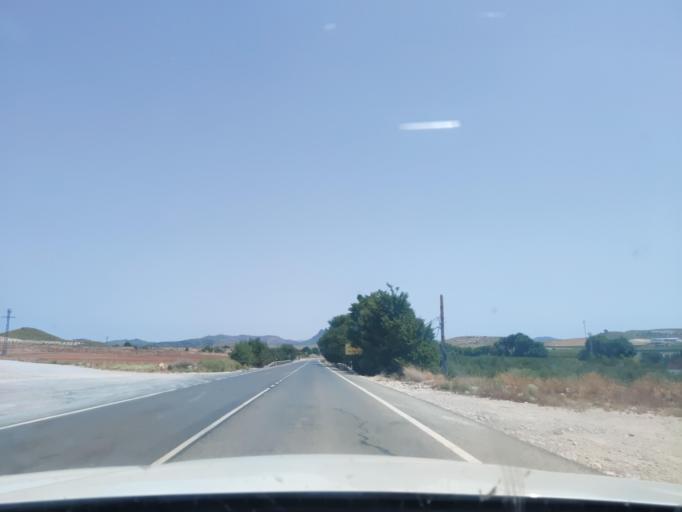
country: ES
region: Castille-La Mancha
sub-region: Provincia de Albacete
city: Hellin
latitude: 38.4956
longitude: -1.6481
